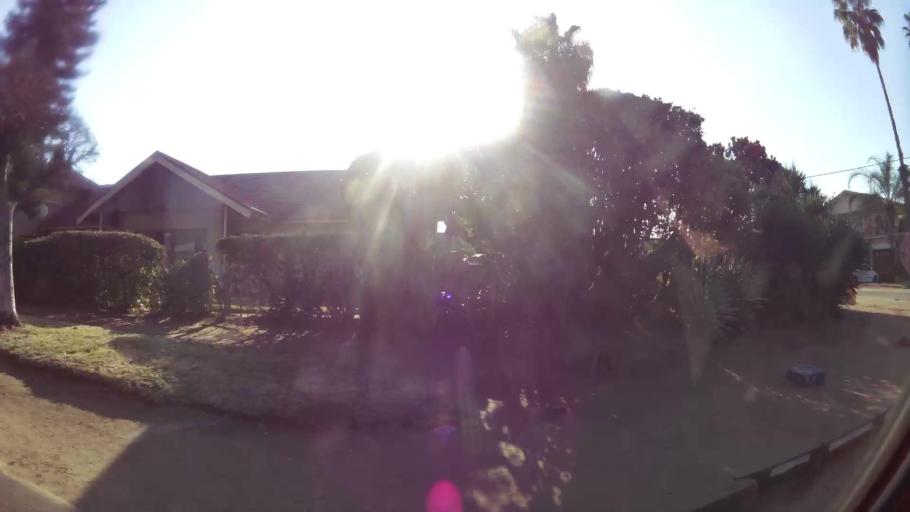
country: ZA
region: North-West
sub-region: Bojanala Platinum District Municipality
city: Rustenburg
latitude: -25.6515
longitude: 27.2424
